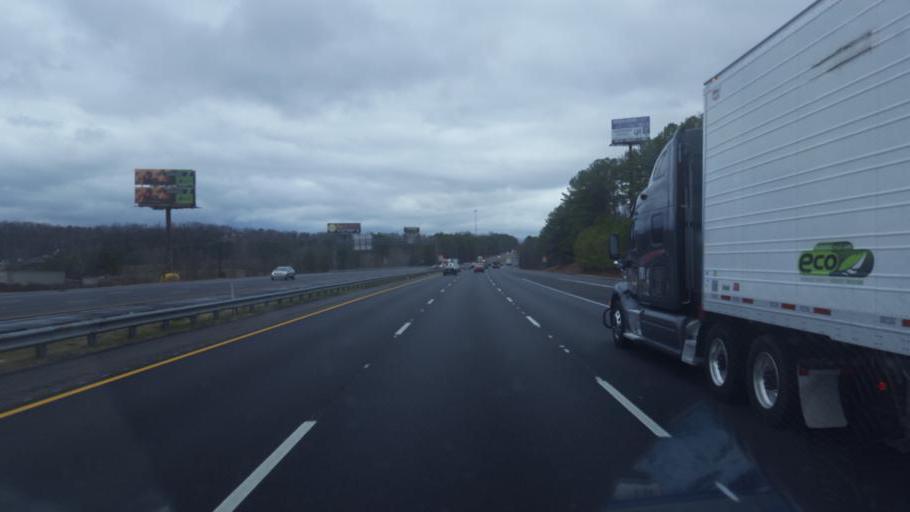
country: US
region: Georgia
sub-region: Whitfield County
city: Varnell
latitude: 34.8626
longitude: -85.0287
